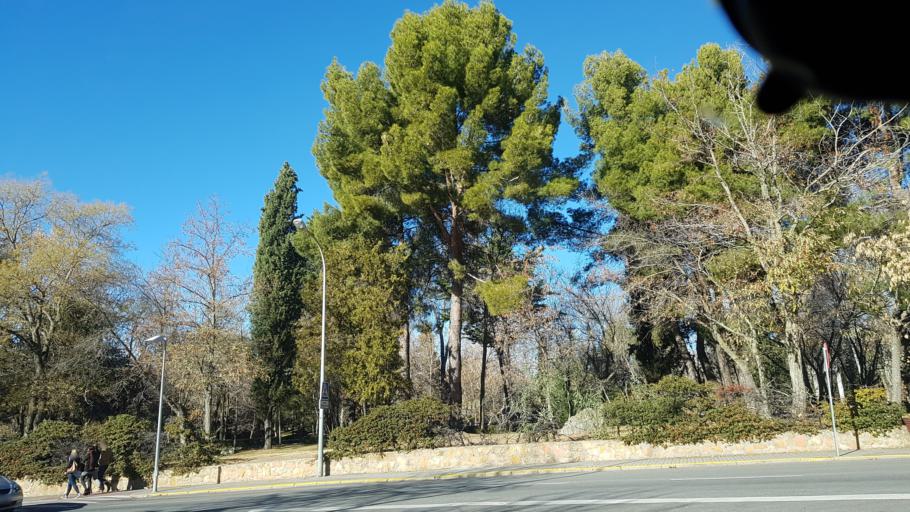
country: ES
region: Castille and Leon
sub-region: Provincia de Segovia
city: Segovia
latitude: 40.9467
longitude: -4.1105
